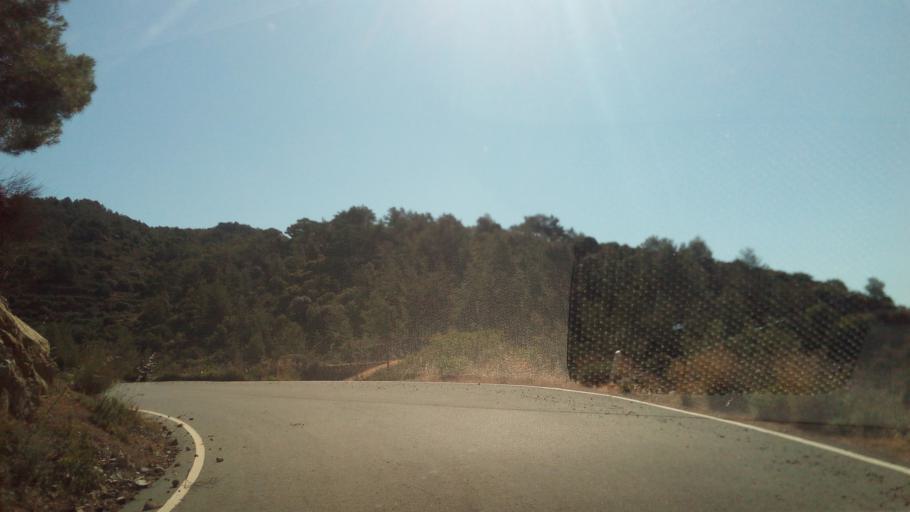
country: CY
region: Lefkosia
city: Lythrodontas
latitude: 34.8890
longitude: 33.2139
